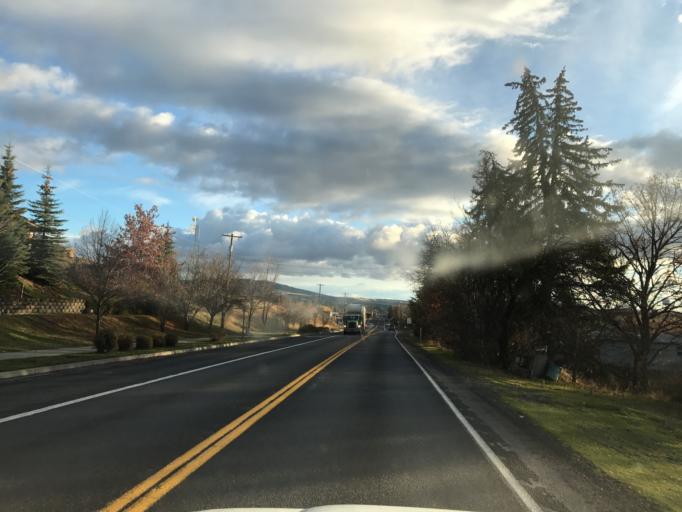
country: US
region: Idaho
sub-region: Latah County
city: Moscow
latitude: 46.7470
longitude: -117.0016
